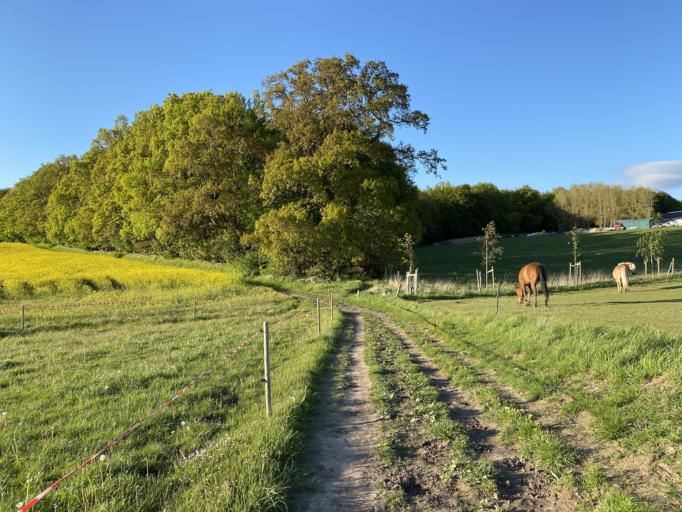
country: DK
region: Capital Region
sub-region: Fureso Kommune
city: Farum
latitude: 55.7951
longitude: 12.3379
